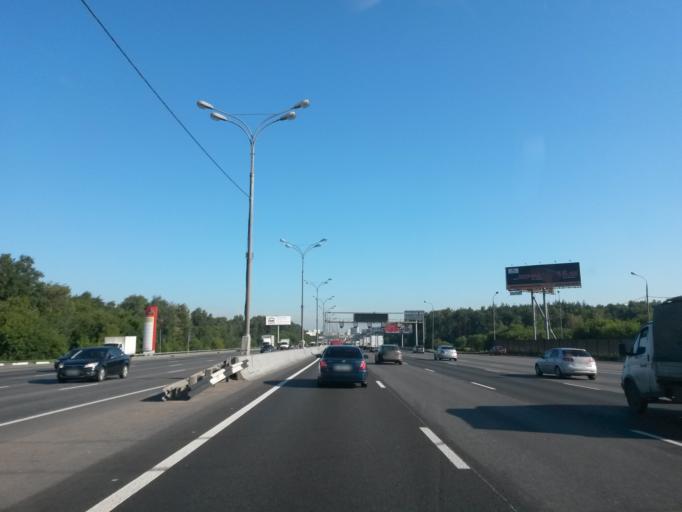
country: RU
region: Moscow
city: Zhulebino
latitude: 55.6699
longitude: 37.8371
